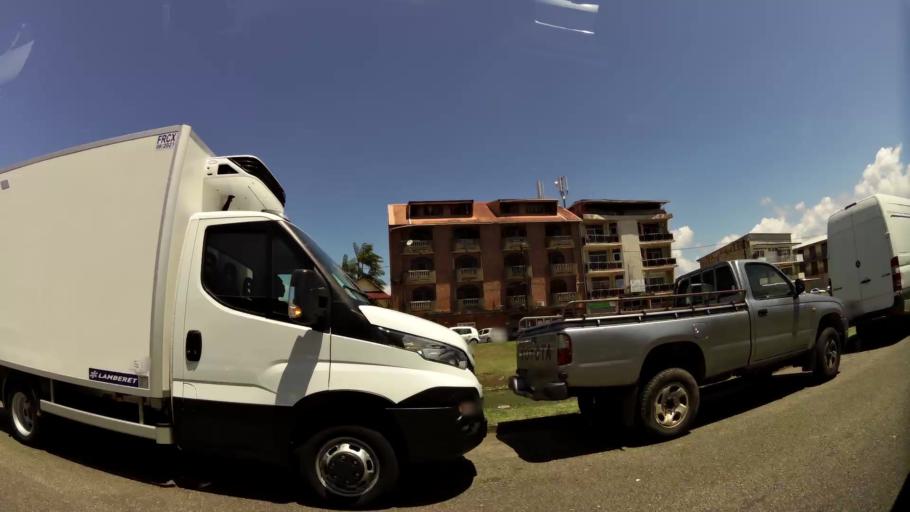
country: GF
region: Guyane
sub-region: Guyane
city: Cayenne
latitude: 4.9357
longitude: -52.3317
